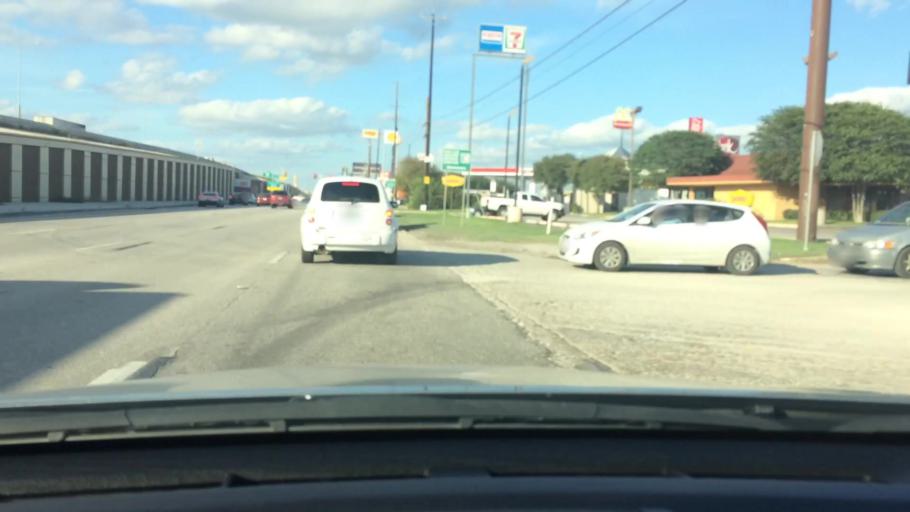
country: US
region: Texas
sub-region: Bexar County
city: Kirby
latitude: 29.4824
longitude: -98.4030
